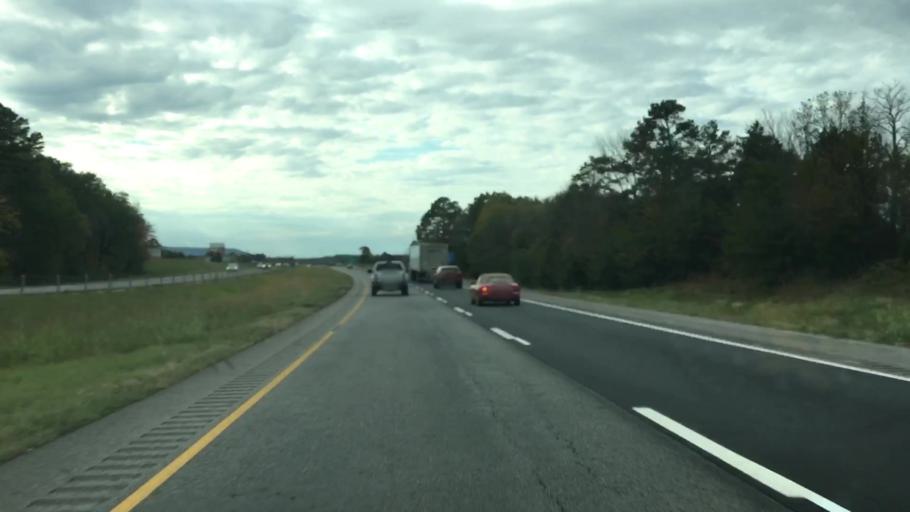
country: US
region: Arkansas
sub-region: Conway County
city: Morrilton
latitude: 35.1741
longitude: -92.7059
